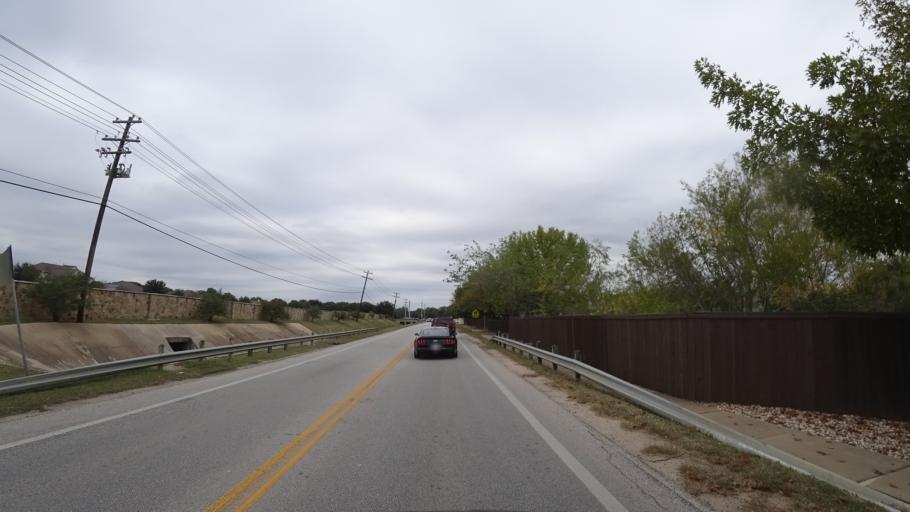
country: US
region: Texas
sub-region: Travis County
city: Shady Hollow
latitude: 30.1512
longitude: -97.8561
